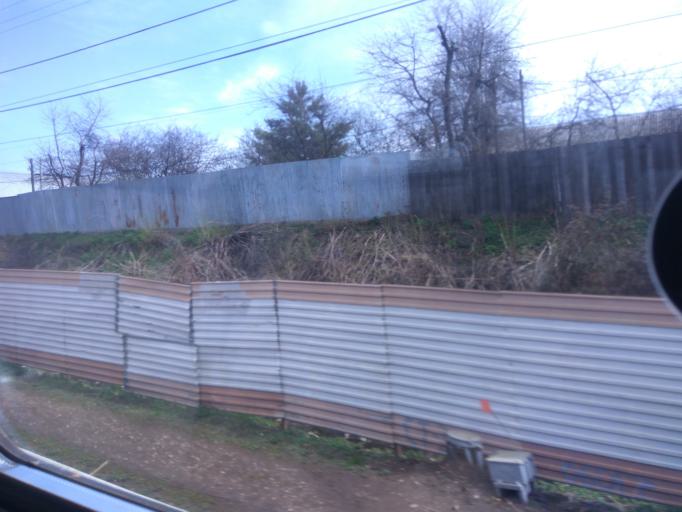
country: RU
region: Moskovskaya
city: Lobnya
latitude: 56.0082
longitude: 37.4876
